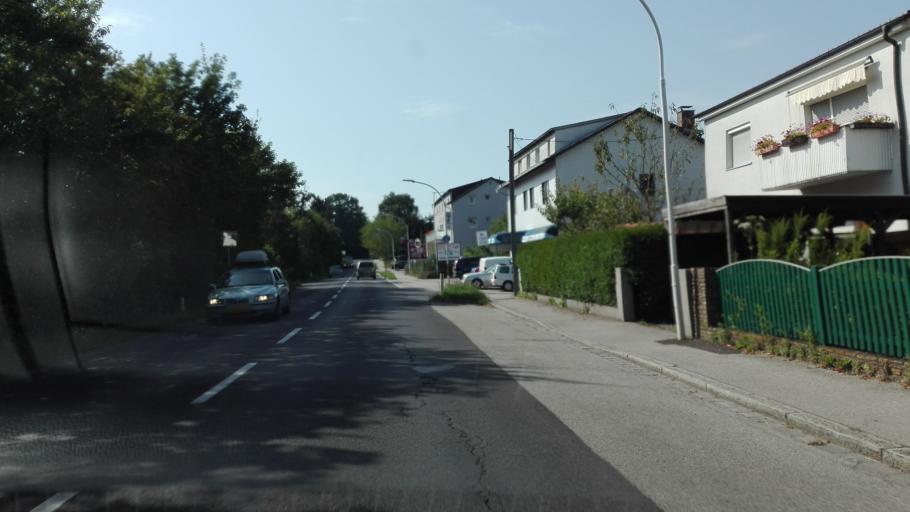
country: AT
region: Upper Austria
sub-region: Politischer Bezirk Linz-Land
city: Leonding
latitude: 48.2579
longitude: 14.2731
